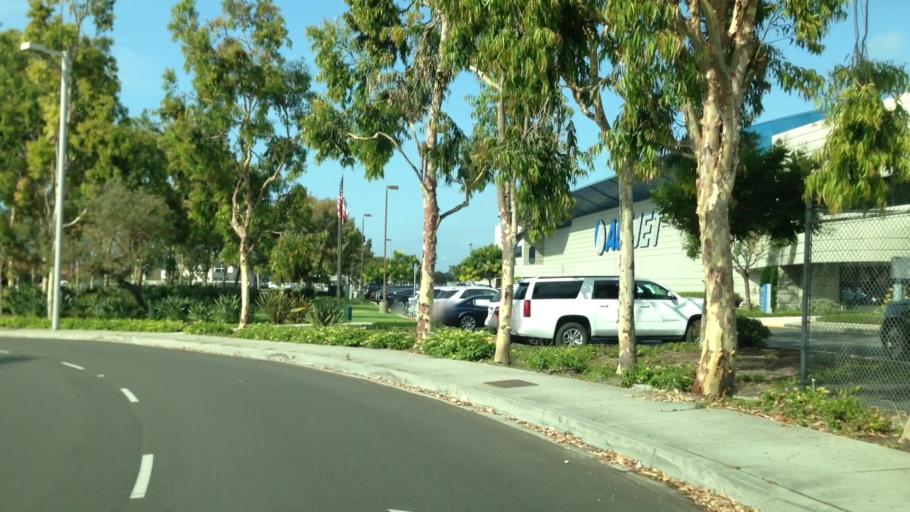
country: US
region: California
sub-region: Orange County
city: Irvine
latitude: 33.6720
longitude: -117.8660
